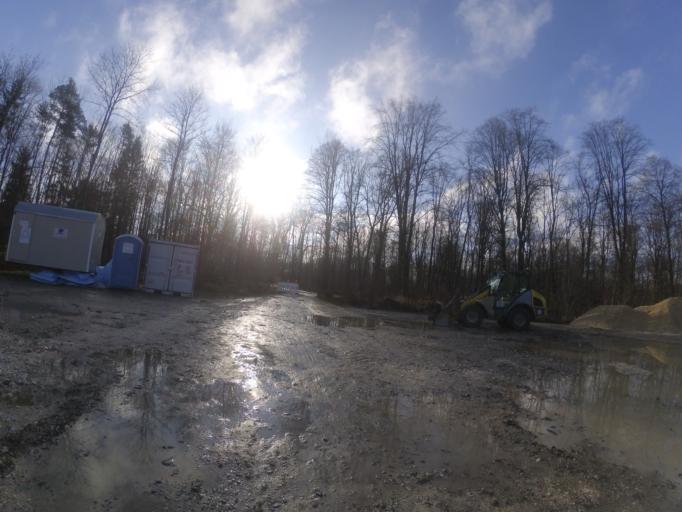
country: DE
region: Bavaria
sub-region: Swabia
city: Neu-Ulm
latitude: 48.4203
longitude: 10.0227
